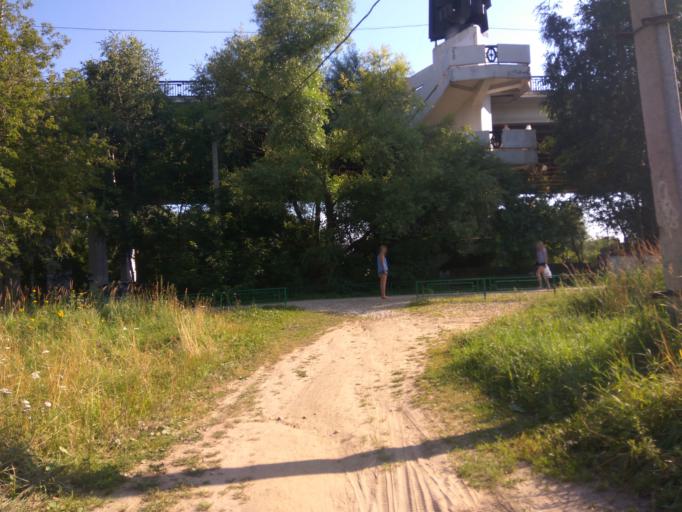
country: RU
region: Moscow
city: Shchukino
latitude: 55.8057
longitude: 37.4440
